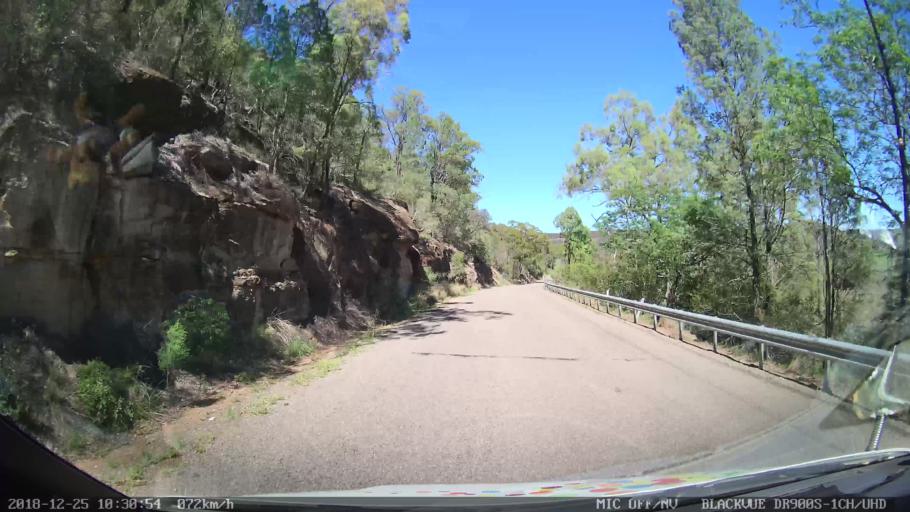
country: AU
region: New South Wales
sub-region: Muswellbrook
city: Denman
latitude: -32.3854
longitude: 150.4340
